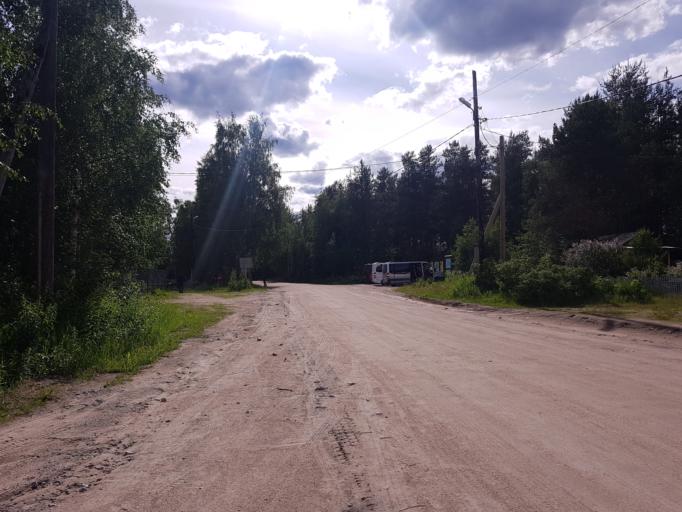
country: RU
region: Republic of Karelia
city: Kostomuksha
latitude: 64.9521
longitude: 30.5511
